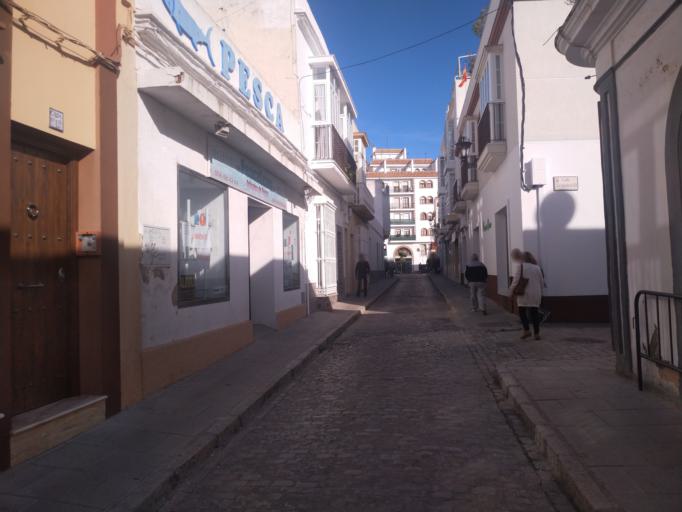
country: ES
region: Andalusia
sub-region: Provincia de Cadiz
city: San Fernando
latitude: 36.4668
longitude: -6.1982
